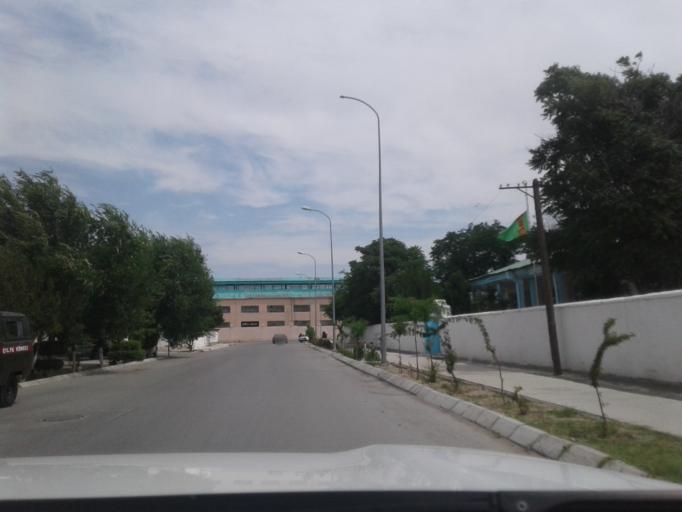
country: TM
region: Balkan
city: Serdar
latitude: 38.9760
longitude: 56.2736
